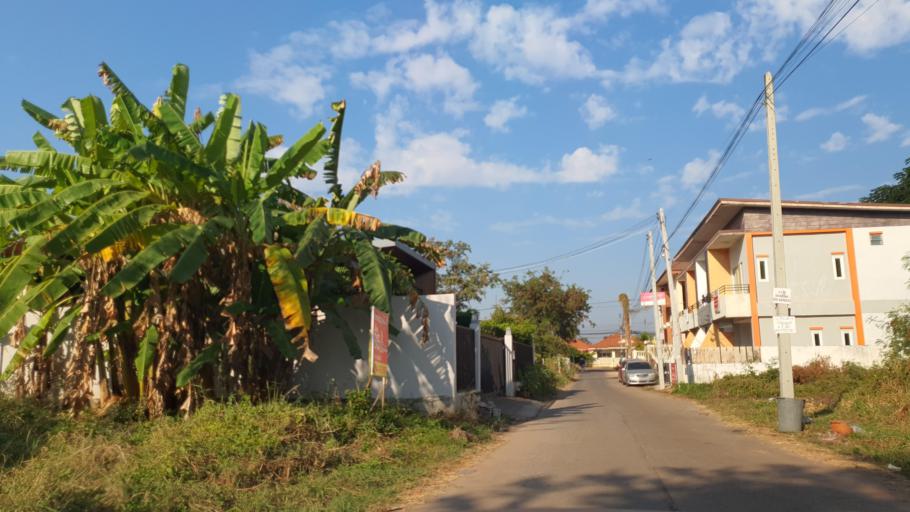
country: TH
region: Khon Kaen
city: Khon Kaen
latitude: 16.4151
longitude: 102.8044
